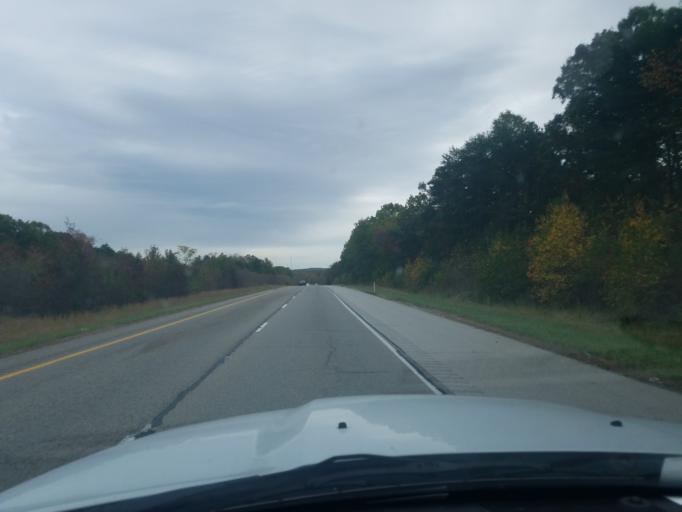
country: US
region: Indiana
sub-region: Warrick County
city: Boonville
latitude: 38.2001
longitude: -87.1891
